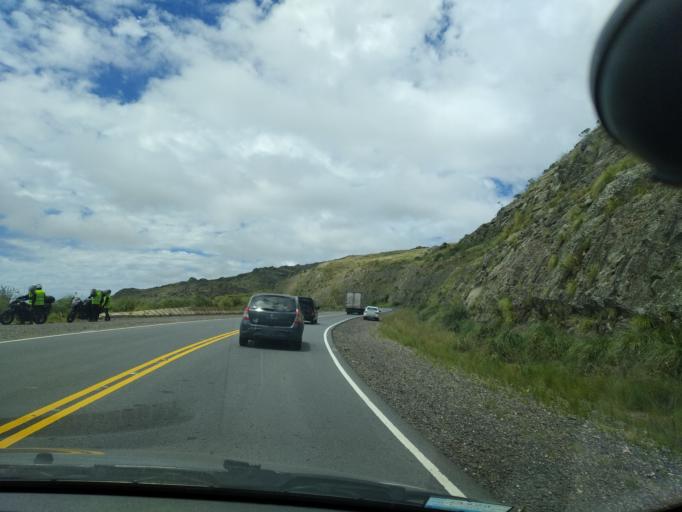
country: AR
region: Cordoba
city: Cuesta Blanca
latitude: -31.6028
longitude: -64.6956
